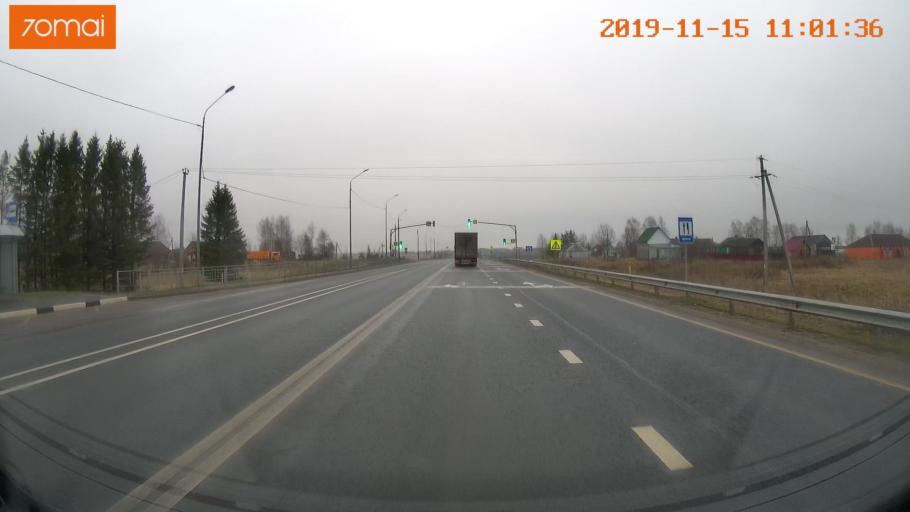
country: RU
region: Vologda
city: Chebsara
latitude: 59.1322
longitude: 38.9237
